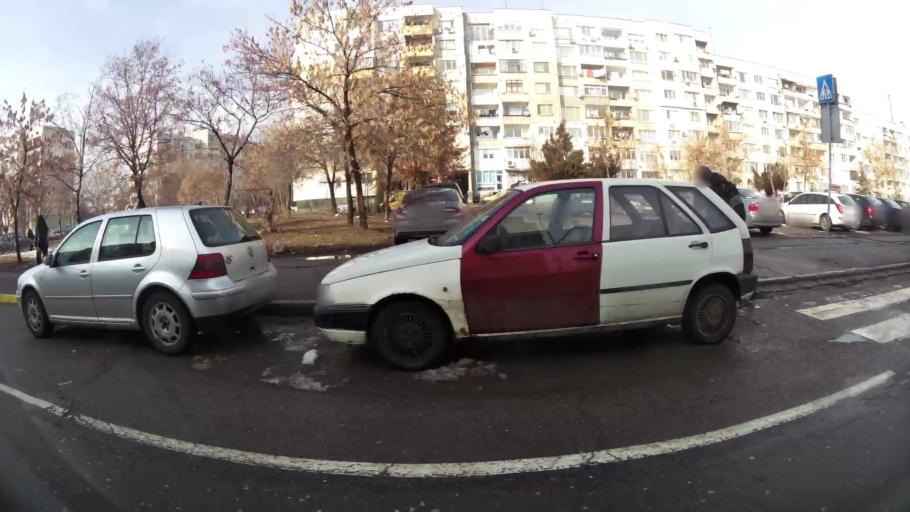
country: BG
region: Sofia-Capital
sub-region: Stolichna Obshtina
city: Sofia
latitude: 42.7191
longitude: 23.2629
